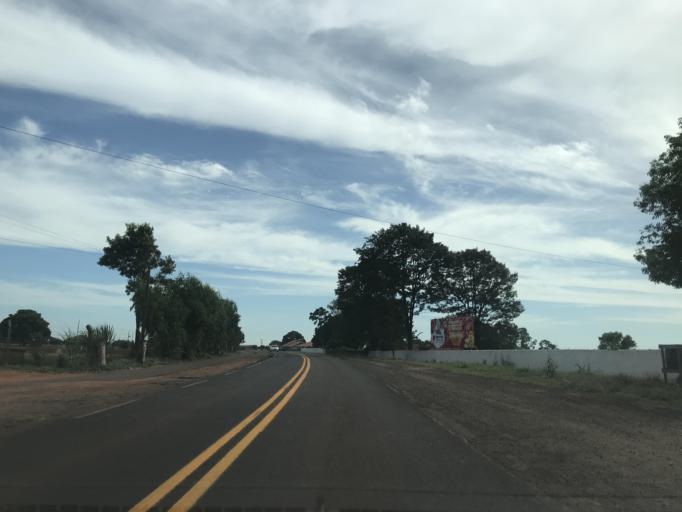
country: BR
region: Parana
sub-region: Terra Rica
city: Terra Rica
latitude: -22.7525
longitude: -52.6261
